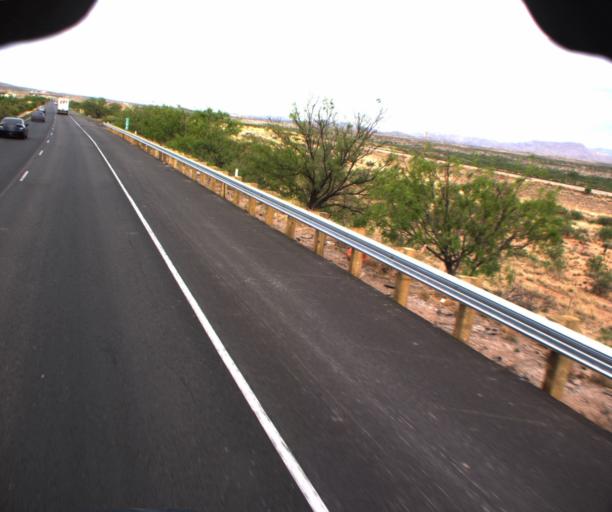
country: US
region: Arizona
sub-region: Cochise County
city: Mescal
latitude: 31.9792
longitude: -110.5193
